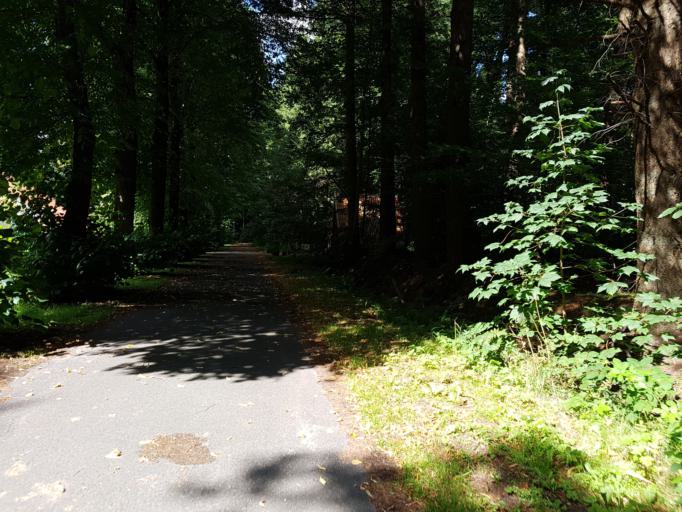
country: DE
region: Lower Saxony
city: Friedeburg
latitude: 53.4916
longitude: 7.8180
